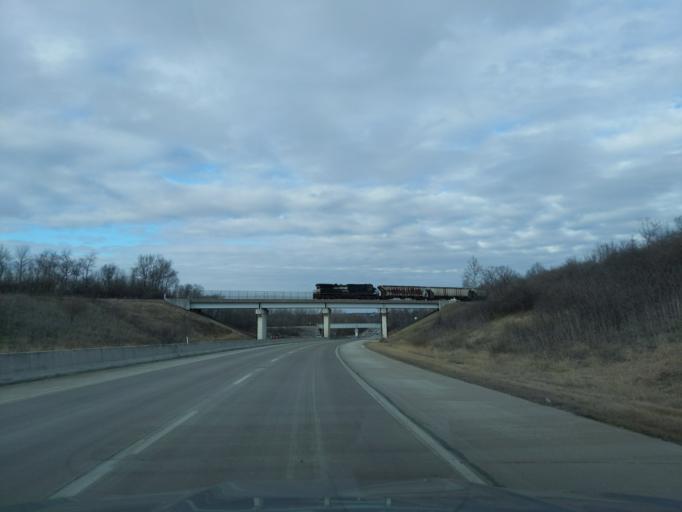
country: US
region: Indiana
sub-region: Tippecanoe County
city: Shadeland
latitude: 40.3932
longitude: -86.9212
